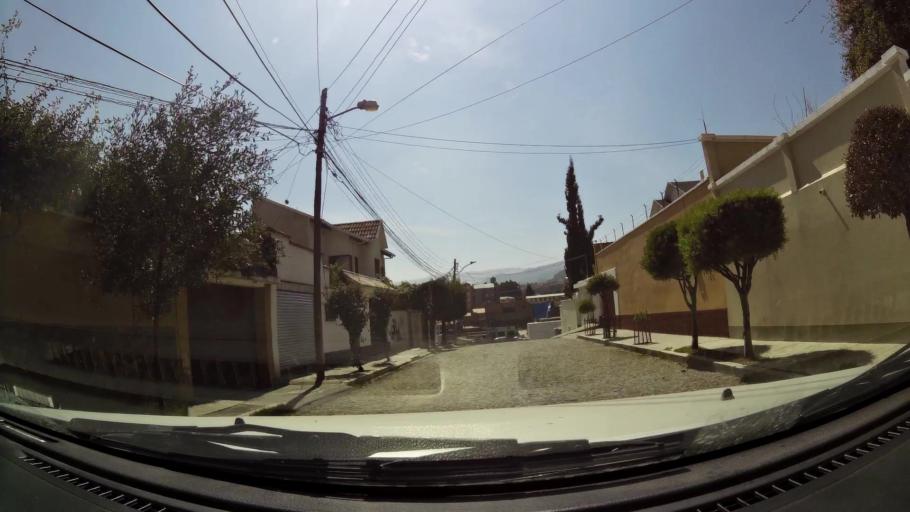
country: BO
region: La Paz
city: La Paz
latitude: -16.5425
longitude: -68.0597
